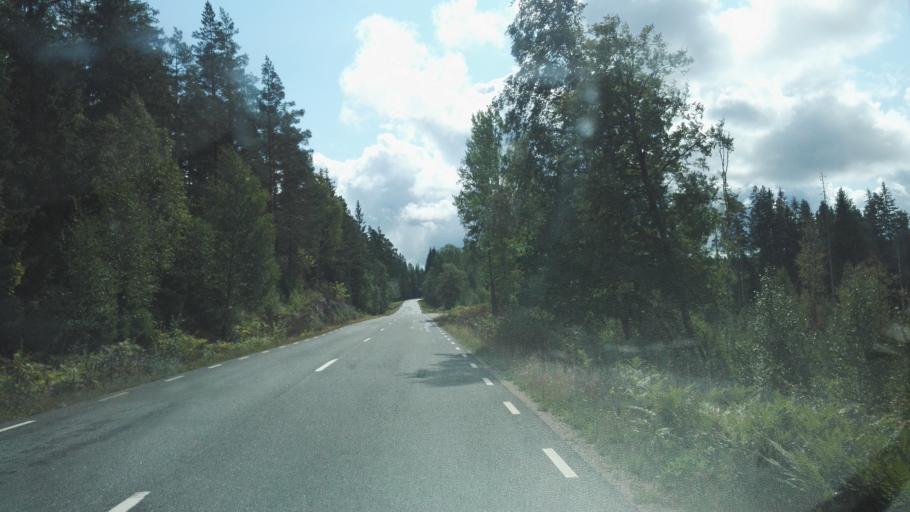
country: SE
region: Joenkoeping
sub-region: Vetlanda Kommun
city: Landsbro
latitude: 57.2542
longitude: 14.9406
